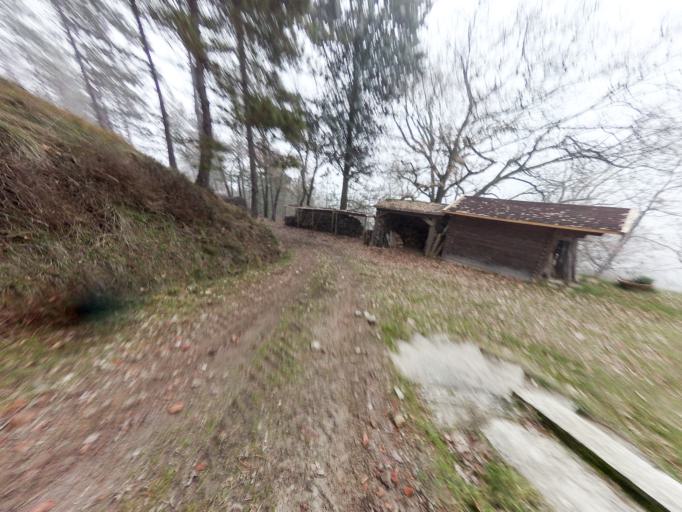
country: IT
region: Emilia-Romagna
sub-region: Provincia di Bologna
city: Pianoro
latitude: 44.3381
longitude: 11.3240
